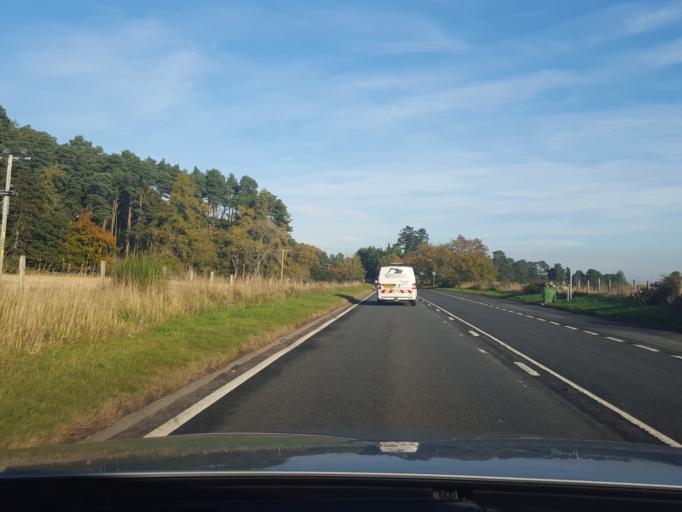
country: GB
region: Scotland
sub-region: Highland
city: Inverness
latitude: 57.4521
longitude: -4.2796
